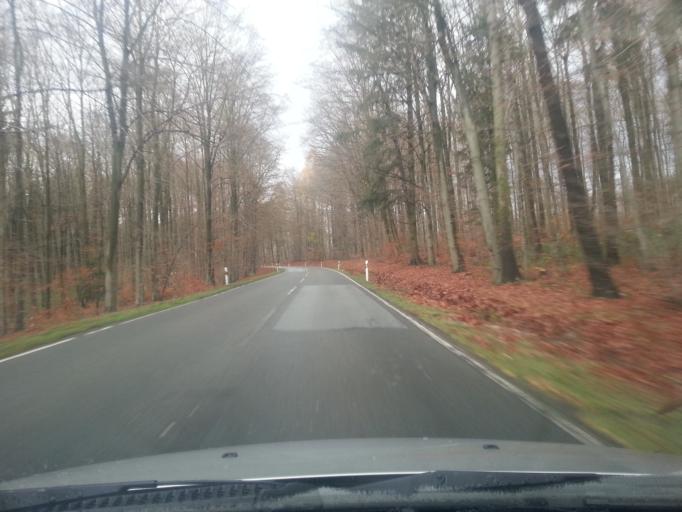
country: DE
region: Baden-Wuerttemberg
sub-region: Karlsruhe Region
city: Gaiberg
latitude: 49.3524
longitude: 8.7495
